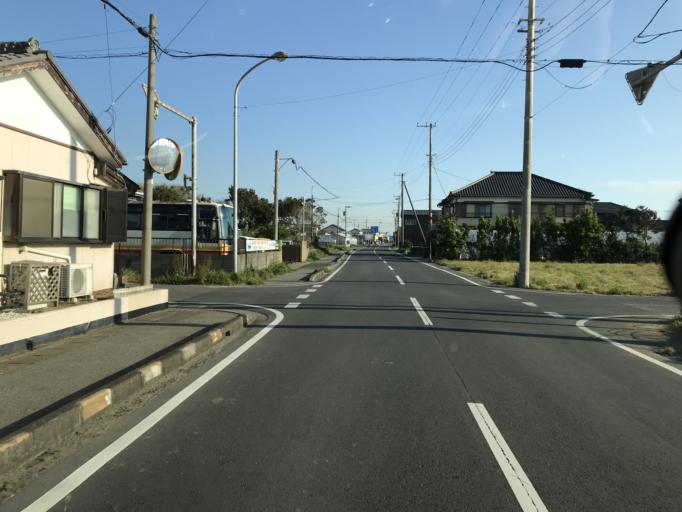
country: JP
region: Chiba
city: Asahi
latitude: 35.7097
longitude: 140.6889
